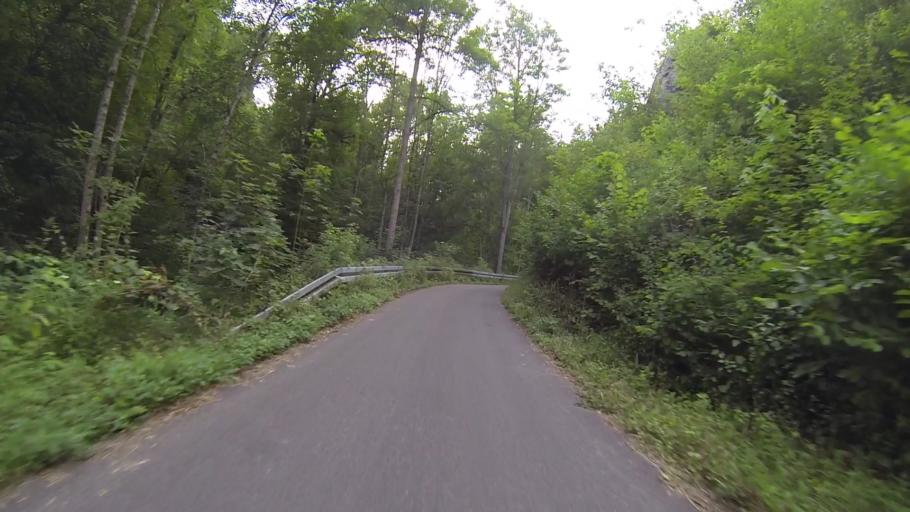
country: DE
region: Baden-Wuerttemberg
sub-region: Tuebingen Region
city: Blaubeuren
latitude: 48.4496
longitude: 9.8522
